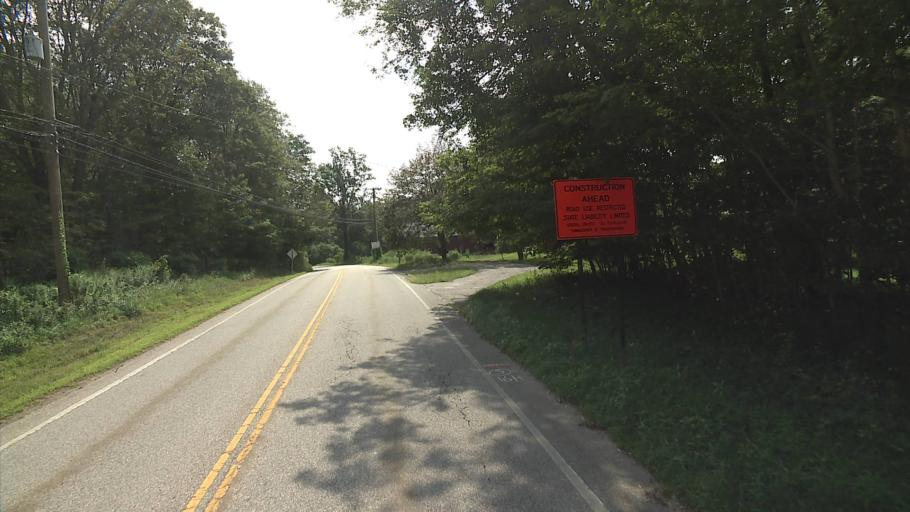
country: US
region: Connecticut
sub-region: Middlesex County
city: East Haddam
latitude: 41.4467
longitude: -72.4280
